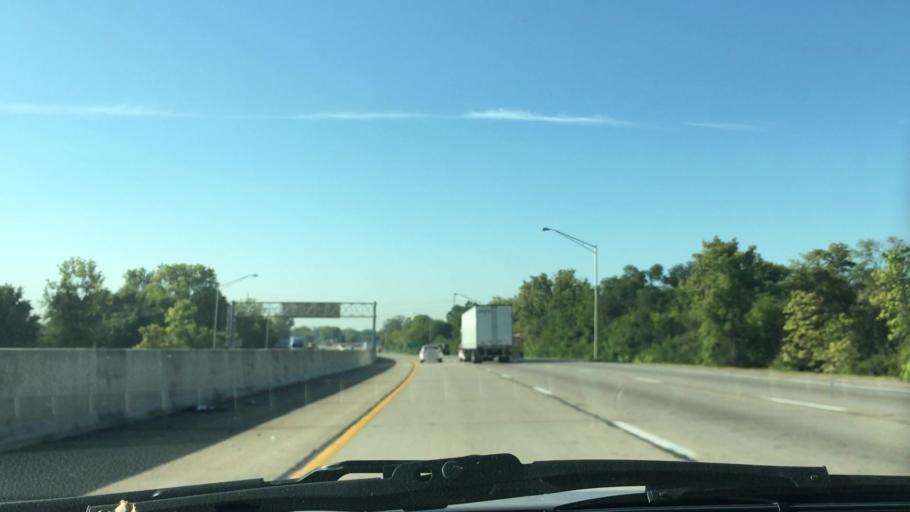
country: US
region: Indiana
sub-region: Marion County
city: Speedway
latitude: 39.7418
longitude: -86.2387
